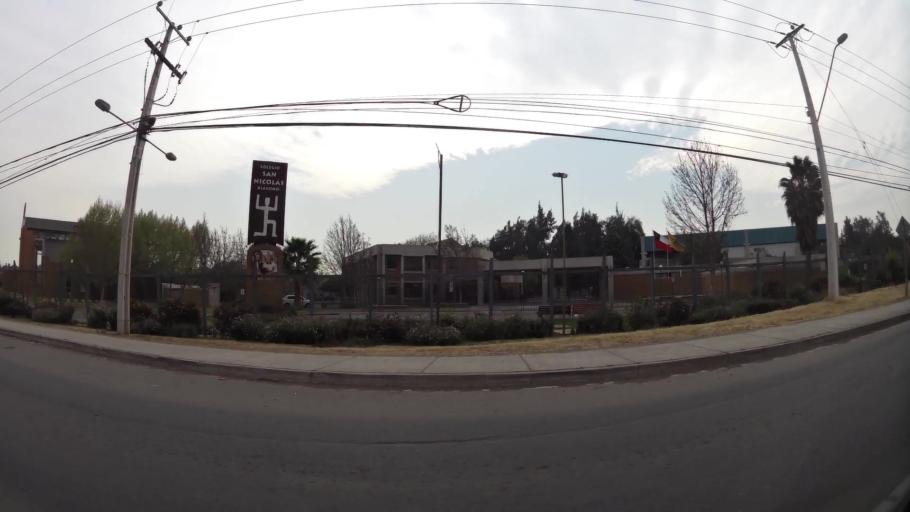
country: CL
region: Santiago Metropolitan
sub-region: Provincia de Chacabuco
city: Chicureo Abajo
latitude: -33.2757
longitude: -70.7025
